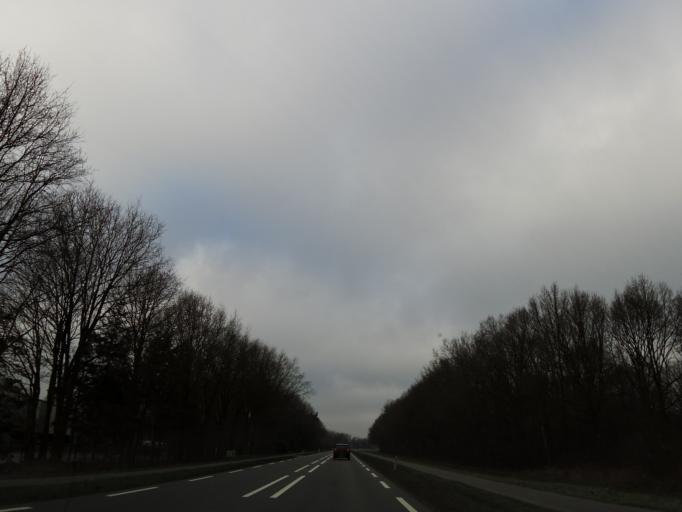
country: NL
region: Limburg
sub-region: Gemeente Venray
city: Venray
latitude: 51.4541
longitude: 5.9463
